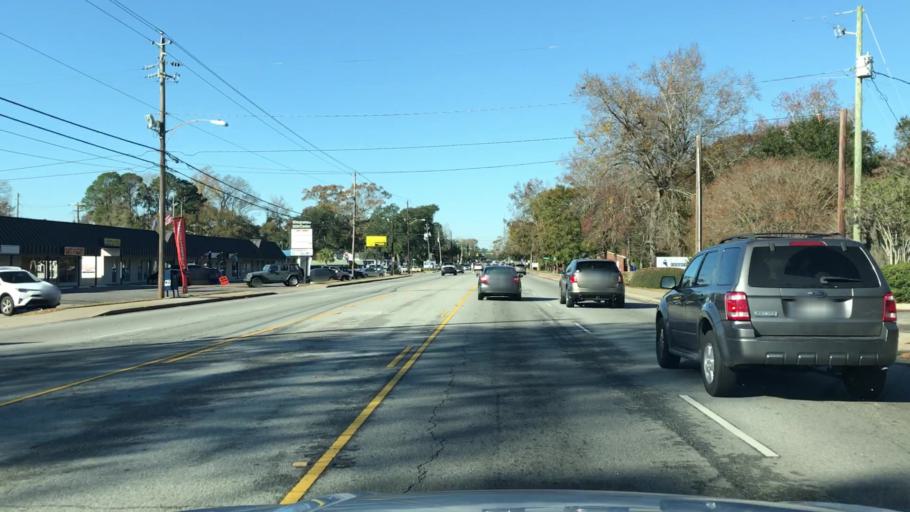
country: US
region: South Carolina
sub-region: Charleston County
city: North Charleston
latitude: 32.7980
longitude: -80.0023
